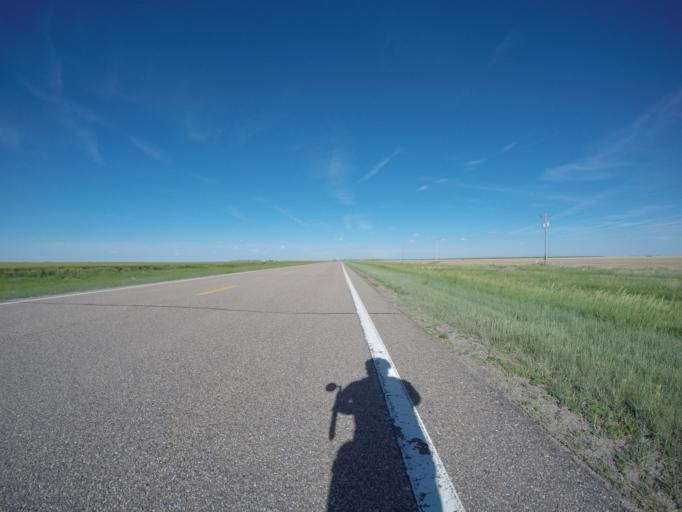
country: US
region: Kansas
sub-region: Cheyenne County
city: Saint Francis
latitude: 39.7566
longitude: -101.9715
